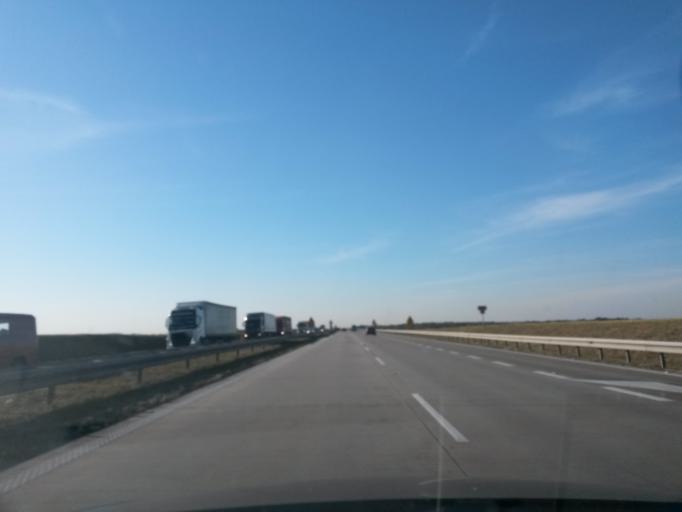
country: PL
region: Lower Silesian Voivodeship
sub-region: Powiat sredzki
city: Udanin
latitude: 51.0711
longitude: 16.4651
